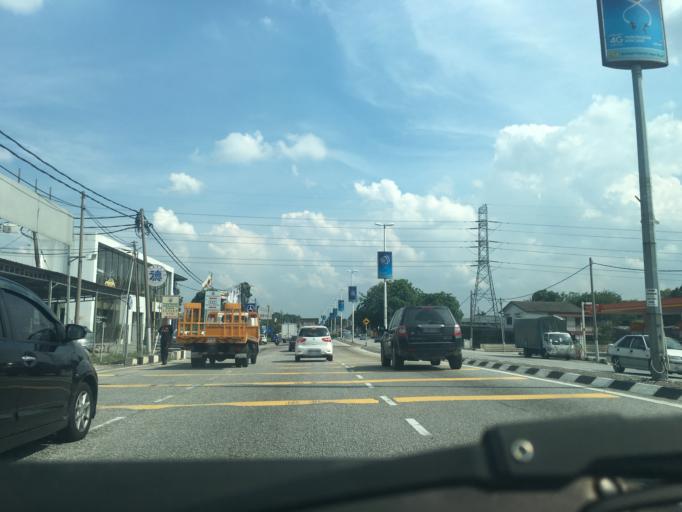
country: MY
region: Perak
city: Ipoh
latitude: 4.6213
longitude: 101.0809
